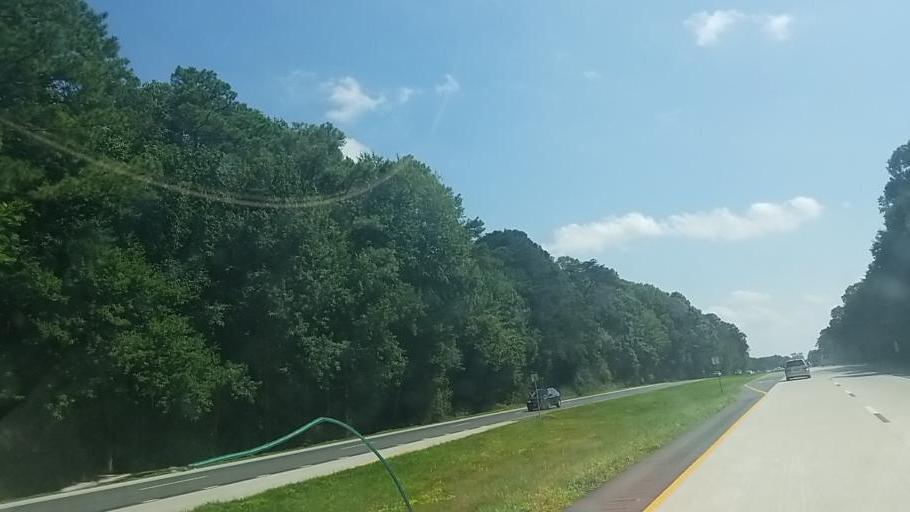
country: US
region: Delaware
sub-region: Sussex County
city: Milford
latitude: 38.8637
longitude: -75.4394
